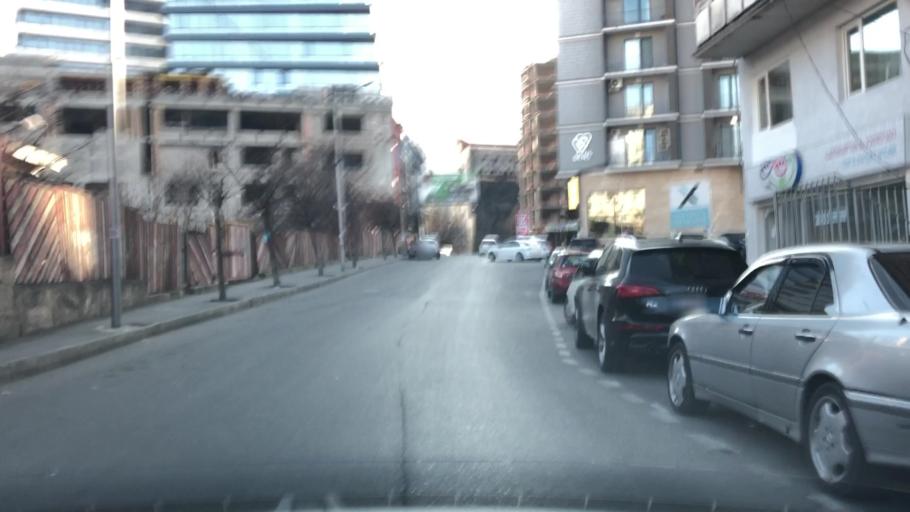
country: GE
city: Tsqnet'i
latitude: 41.7131
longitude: 44.7569
